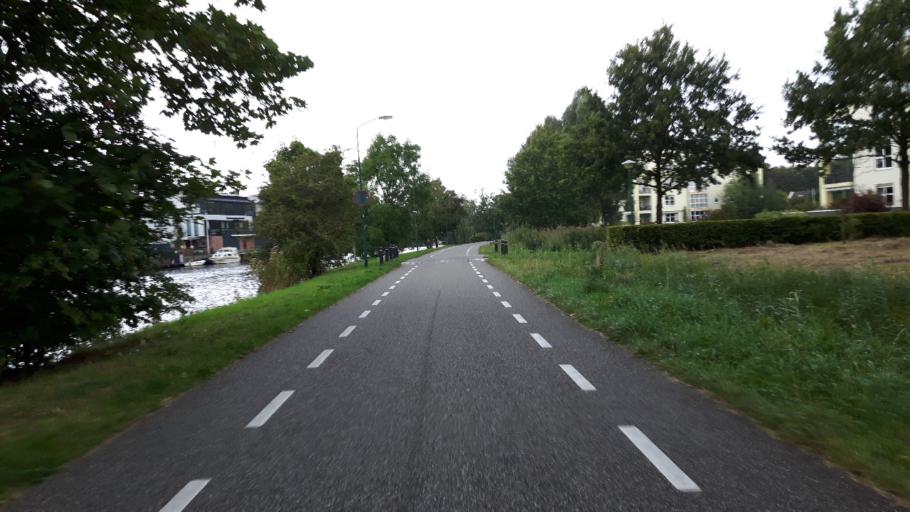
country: NL
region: Utrecht
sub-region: Stichtse Vecht
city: Maarssen
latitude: 52.1334
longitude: 5.0474
